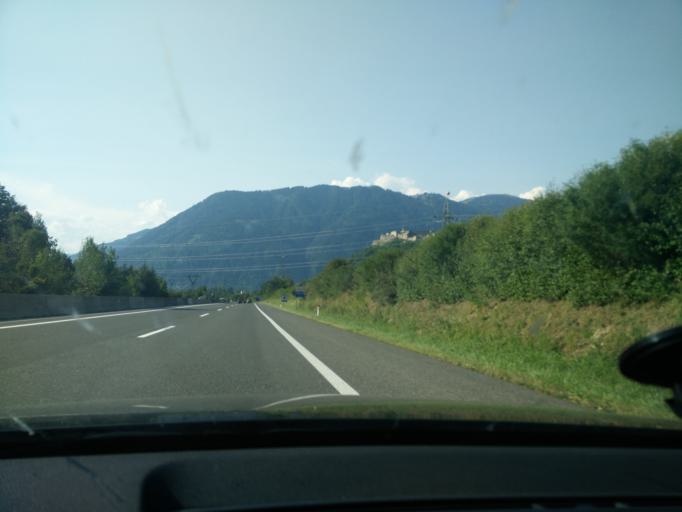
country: AT
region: Carinthia
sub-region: Politischer Bezirk Villach Land
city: Wernberg
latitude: 46.6301
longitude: 13.8962
